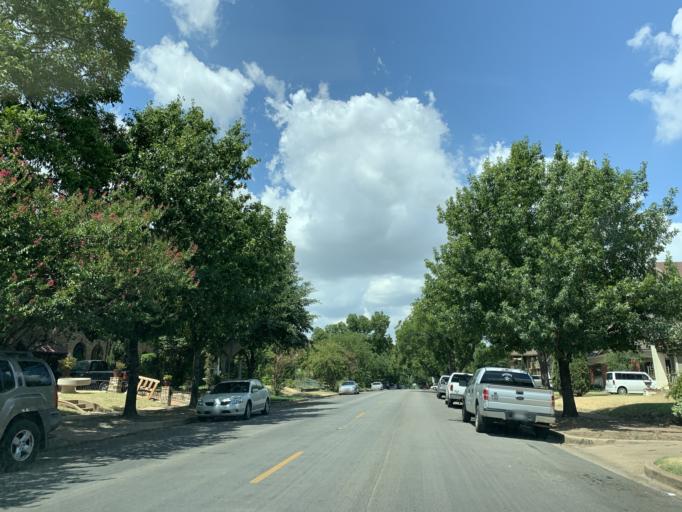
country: US
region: Texas
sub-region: Dallas County
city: Dallas
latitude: 32.7513
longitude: -96.8411
